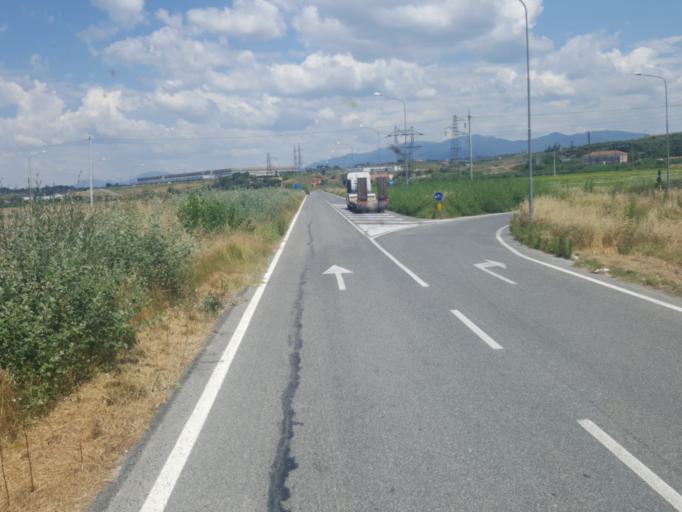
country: IT
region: Latium
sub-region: Citta metropolitana di Roma Capitale
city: Fiano Romano
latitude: 42.1565
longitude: 12.6429
